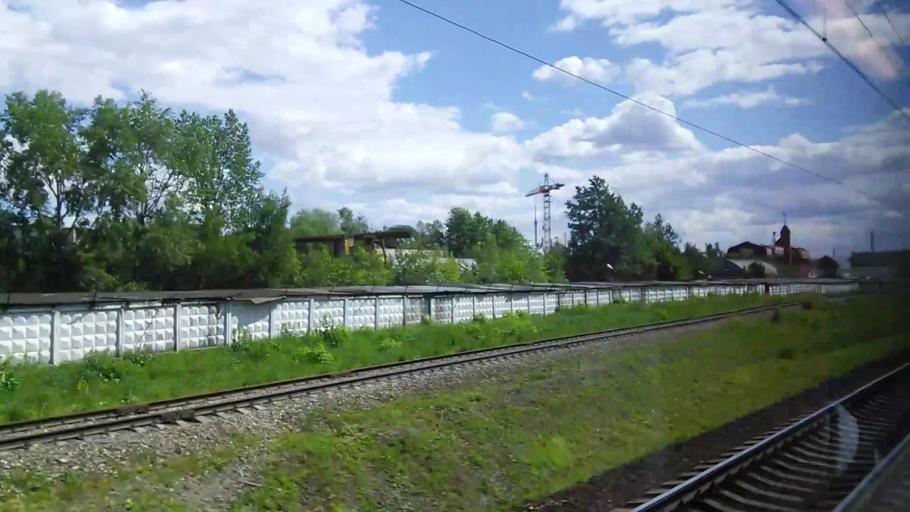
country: RU
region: Moscow
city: Slobodka
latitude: 55.8603
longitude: 37.5747
